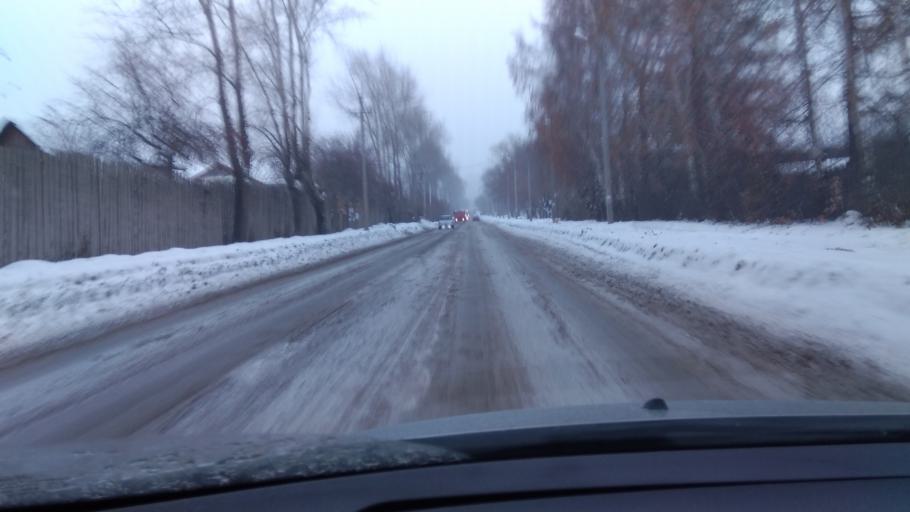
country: RU
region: Sverdlovsk
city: Verkhnyaya Pyshma
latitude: 56.9137
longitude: 60.5817
